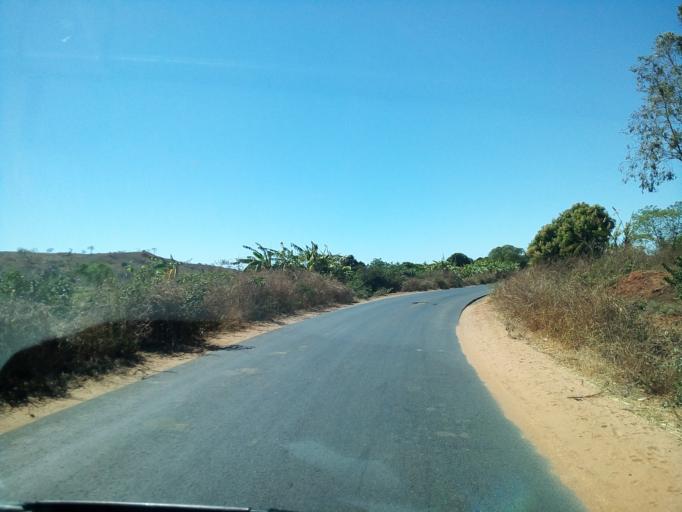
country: MG
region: Boeny
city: Ambato Boeny
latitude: -16.3441
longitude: 46.8736
